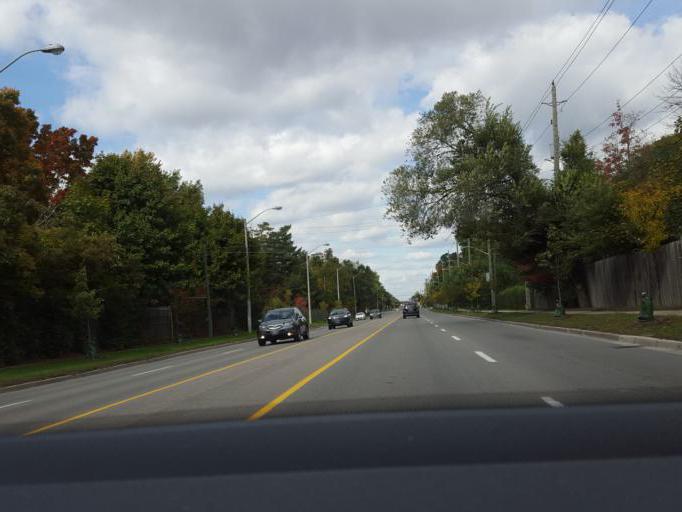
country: CA
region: Ontario
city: Willowdale
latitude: 43.7476
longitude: -79.3589
